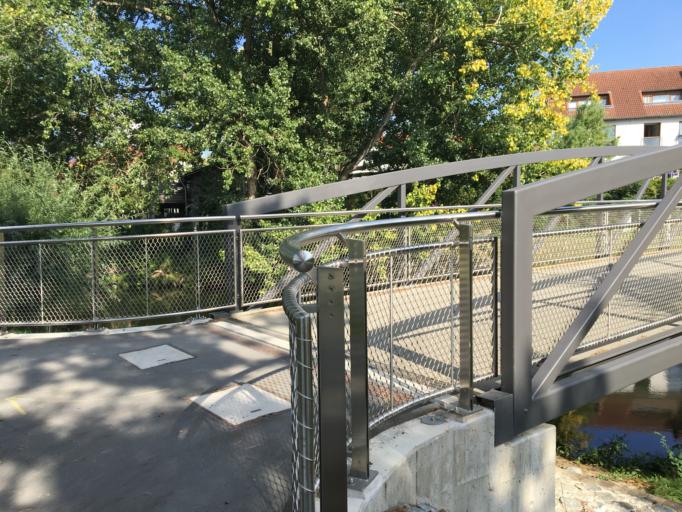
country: DE
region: Lower Saxony
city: Leiferde
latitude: 52.2296
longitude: 10.5184
